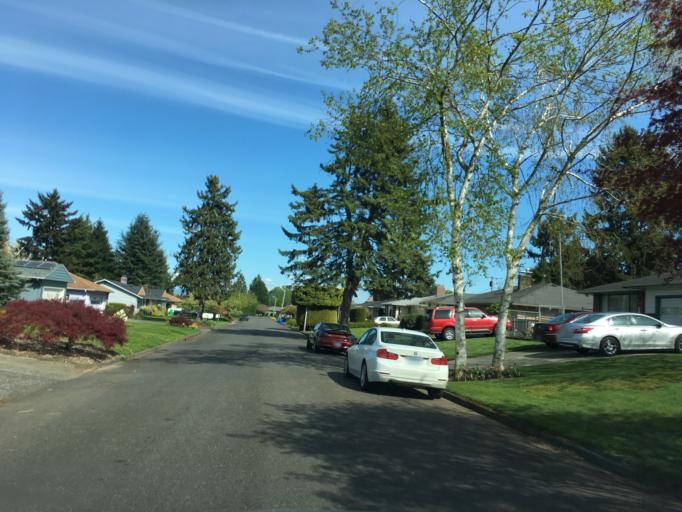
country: US
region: Oregon
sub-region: Multnomah County
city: Lents
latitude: 45.5435
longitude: -122.5352
